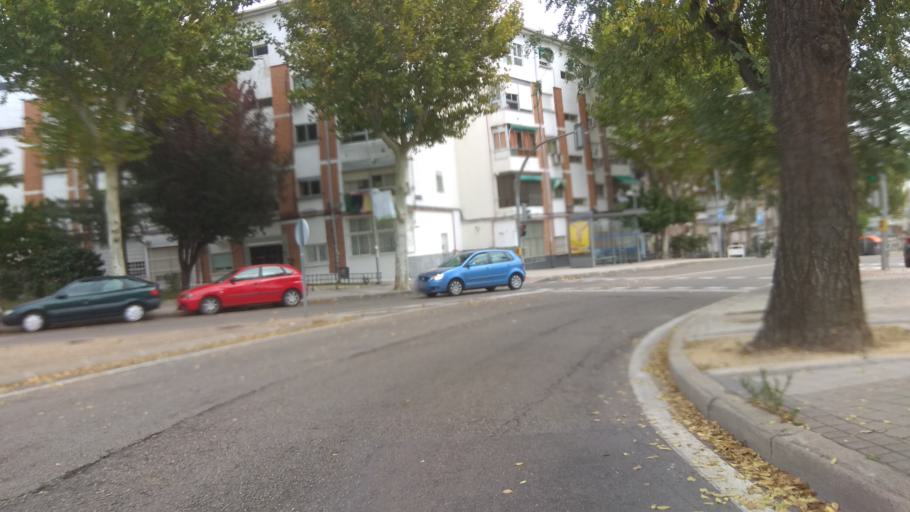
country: ES
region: Madrid
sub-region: Provincia de Madrid
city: Vicalvaro
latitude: 40.4054
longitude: -3.6168
